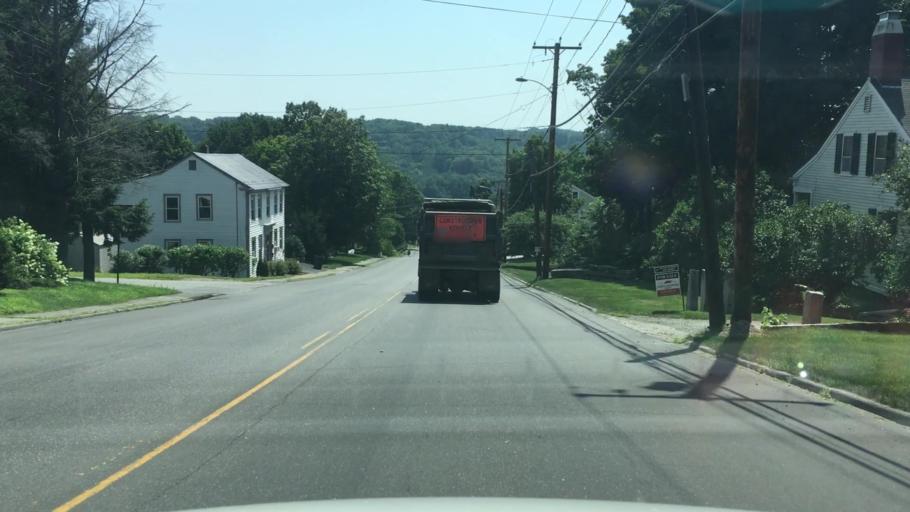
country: US
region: Maine
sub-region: Kennebec County
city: Hallowell
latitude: 44.2892
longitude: -69.7955
